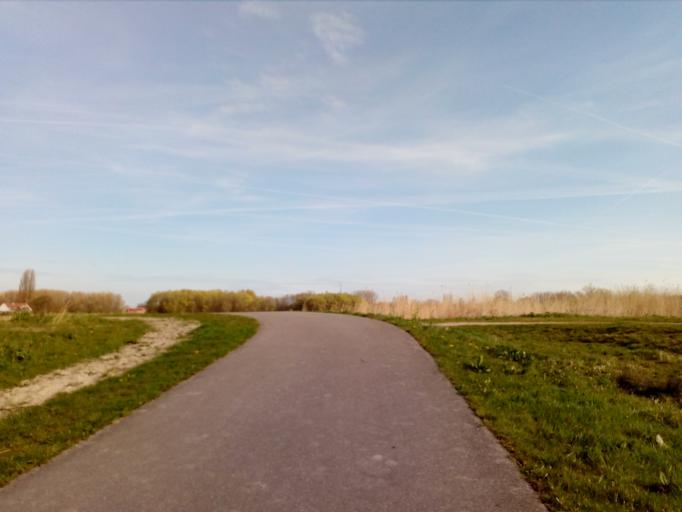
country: NL
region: South Holland
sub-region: Gemeente Schiedam
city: Schiedam
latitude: 51.9511
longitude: 4.3966
